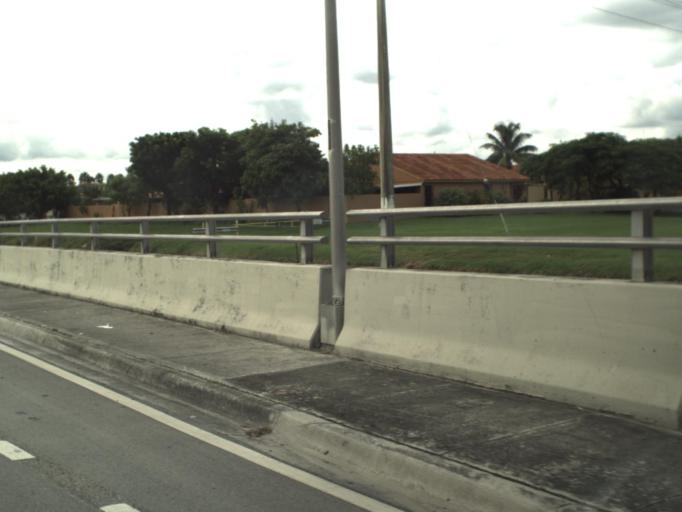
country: US
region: Florida
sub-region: Miami-Dade County
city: Fountainebleau
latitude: 25.7619
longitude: -80.3492
